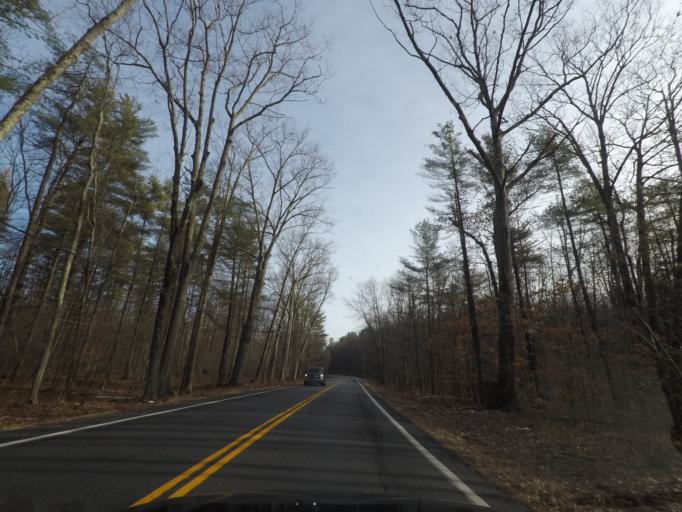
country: US
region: New York
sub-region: Saratoga County
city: Stillwater
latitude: 42.9910
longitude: -73.7085
